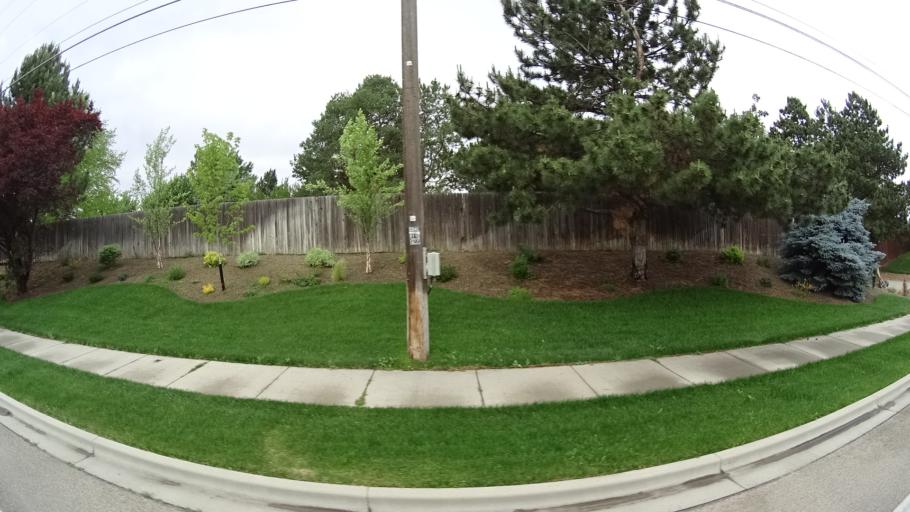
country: US
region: Idaho
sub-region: Ada County
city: Meridian
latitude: 43.5792
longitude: -116.3546
